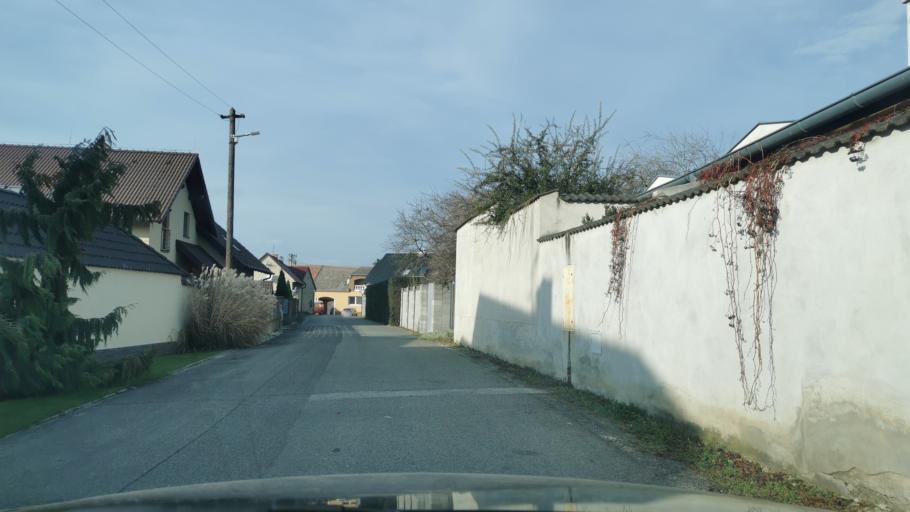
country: SK
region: Trnavsky
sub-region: Okres Skalica
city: Holic
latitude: 48.7924
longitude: 17.1258
